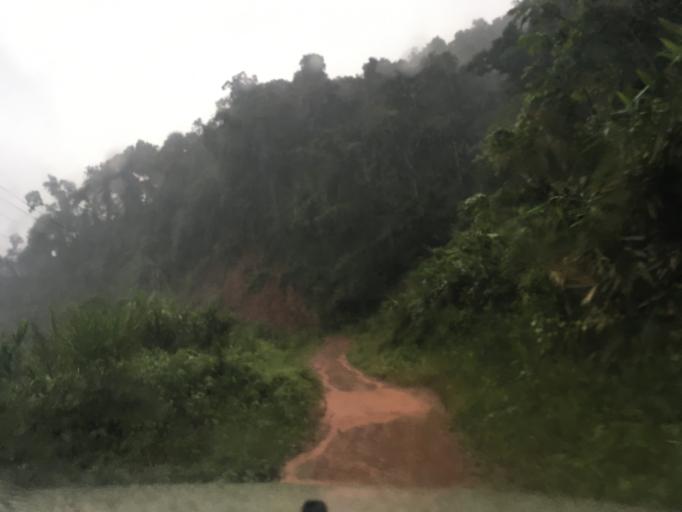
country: LA
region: Oudomxai
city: Muang La
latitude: 21.2291
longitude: 101.9614
